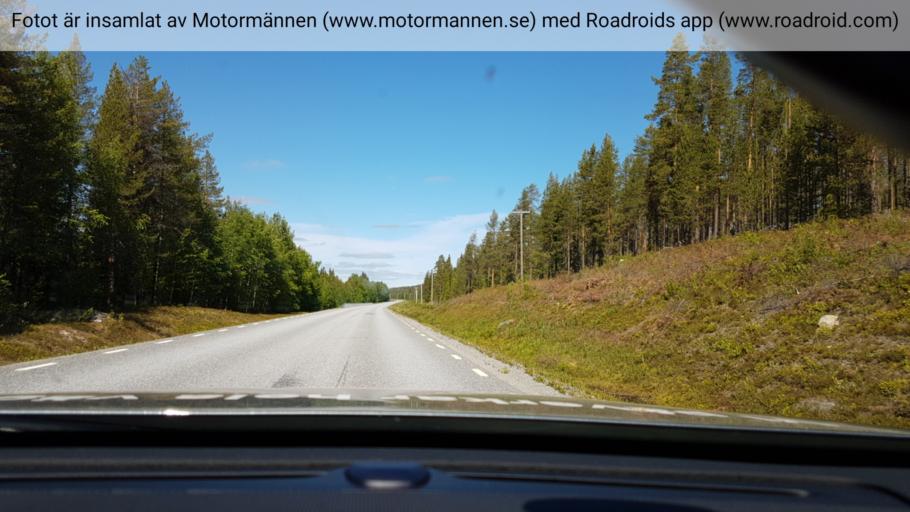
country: SE
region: Vaesterbotten
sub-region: Vilhelmina Kommun
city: Vilhelmina
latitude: 64.3933
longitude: 16.8664
